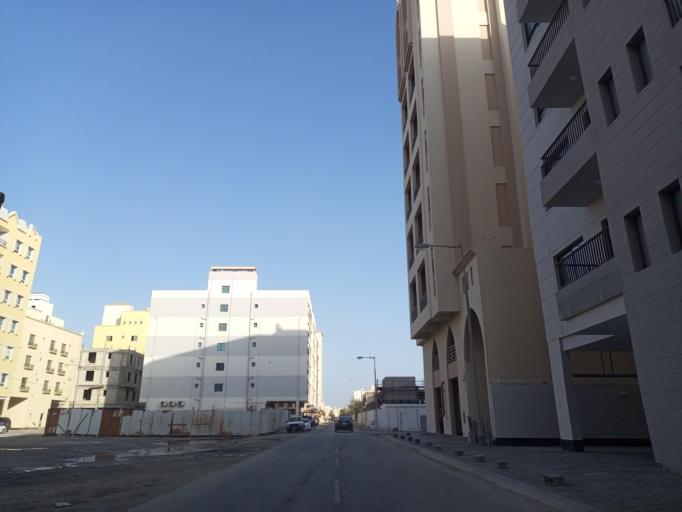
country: BH
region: Muharraq
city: Al Hadd
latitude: 26.2314
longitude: 50.6461
